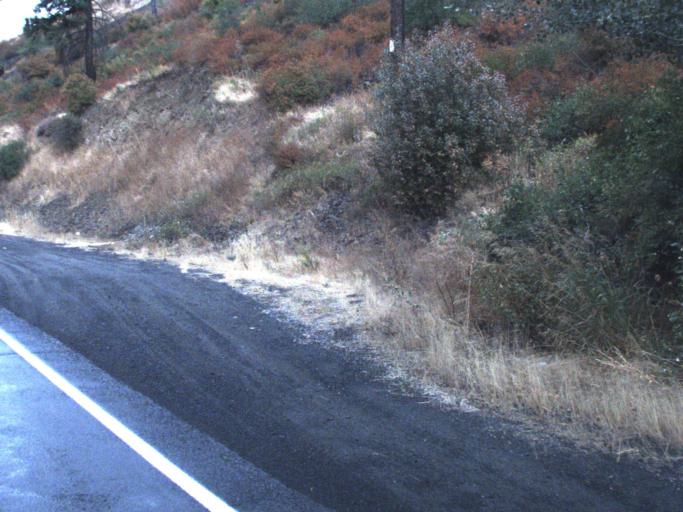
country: US
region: Washington
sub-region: Spokane County
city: Medical Lake
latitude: 47.7513
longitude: -117.8879
